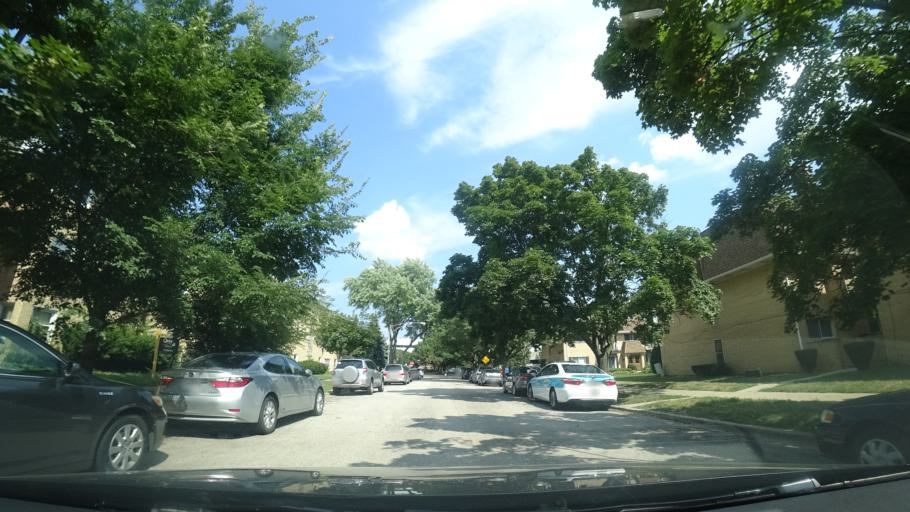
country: US
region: Illinois
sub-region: Cook County
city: Norridge
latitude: 41.9783
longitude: -87.8402
